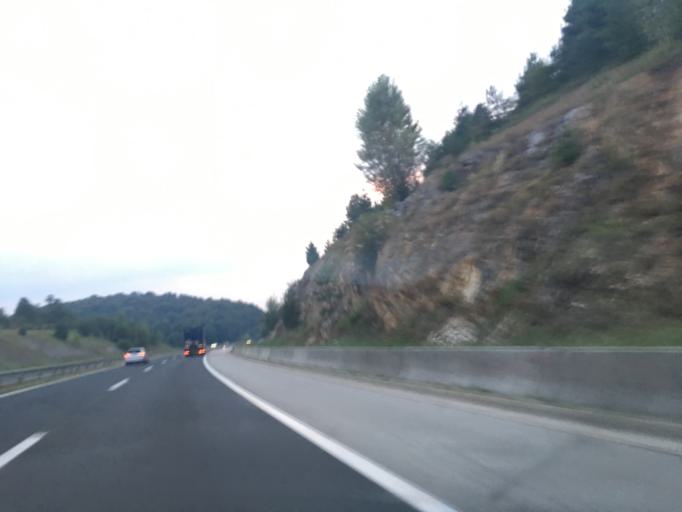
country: HR
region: Karlovacka
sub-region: Grad Karlovac
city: Karlovac
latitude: 45.4906
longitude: 15.4457
